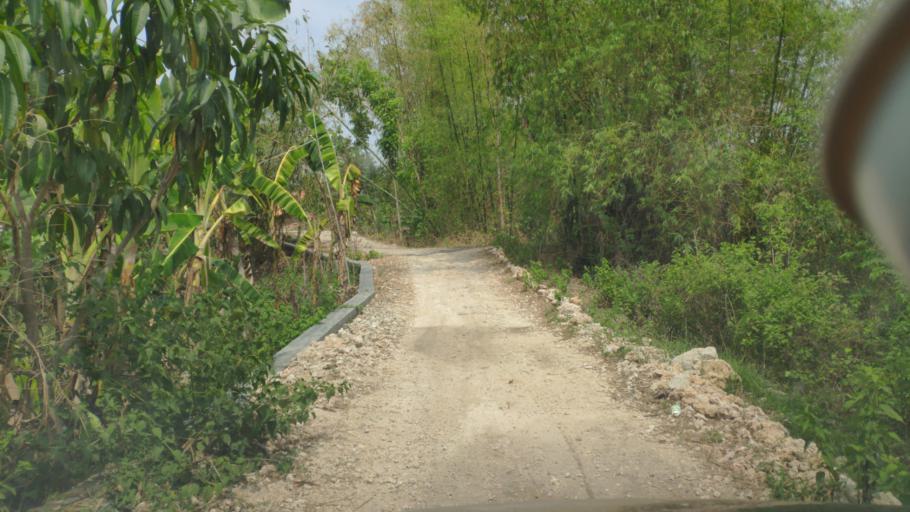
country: ID
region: Central Java
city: Karangtalun
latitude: -7.0199
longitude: 111.3613
